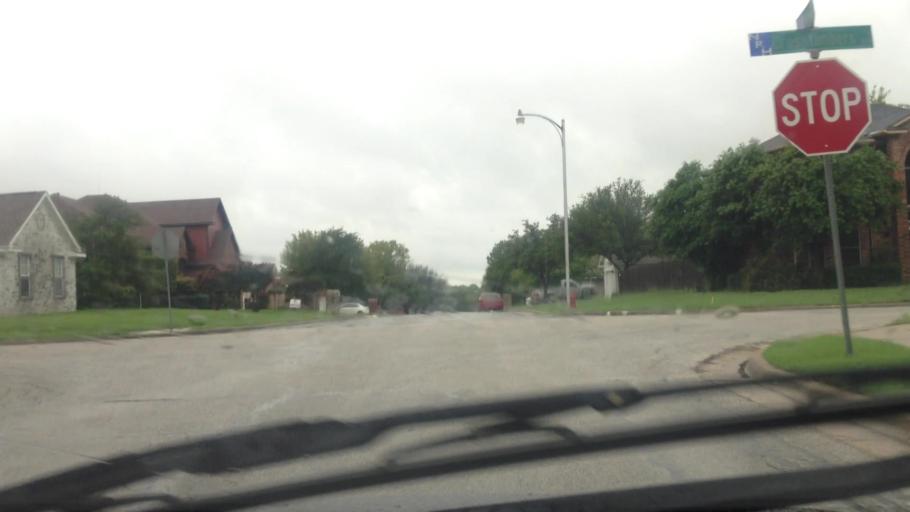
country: US
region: Texas
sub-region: Tarrant County
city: Watauga
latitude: 32.8879
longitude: -97.2346
